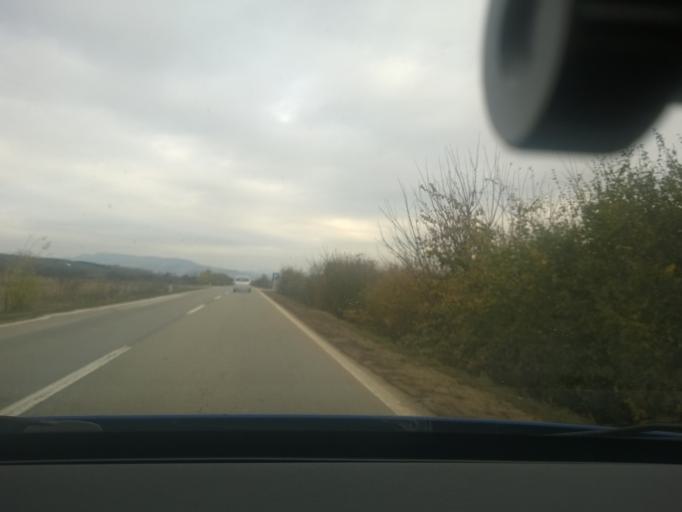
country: RS
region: Central Serbia
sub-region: Pirotski Okrug
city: Pirot
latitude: 43.0841
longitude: 22.6591
